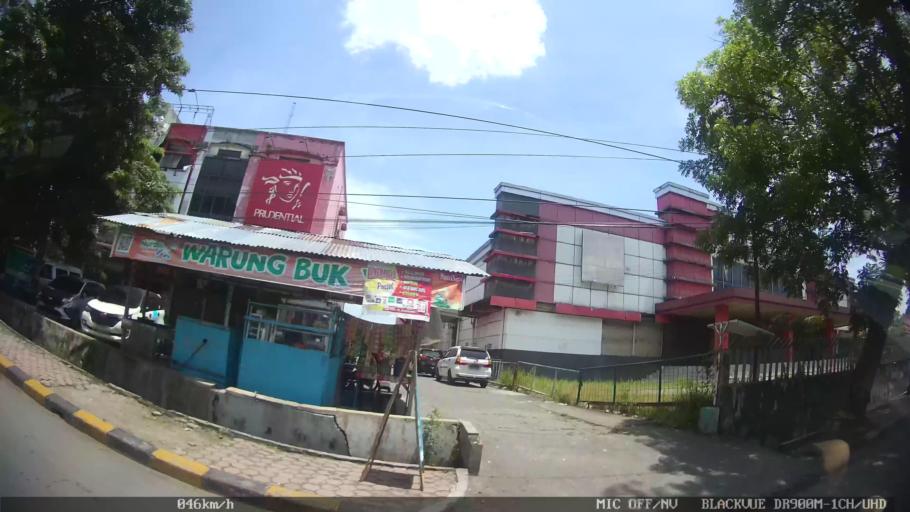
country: ID
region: North Sumatra
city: Binjai
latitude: 3.6091
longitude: 98.4950
